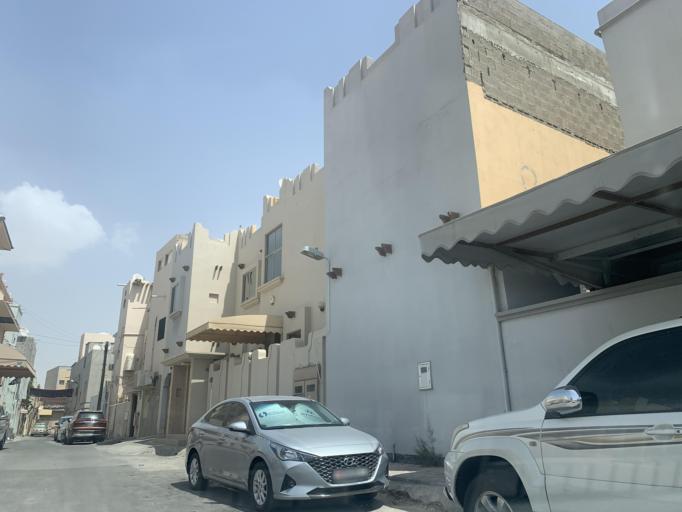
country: BH
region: Central Governorate
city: Madinat Hamad
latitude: 26.1463
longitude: 50.4966
